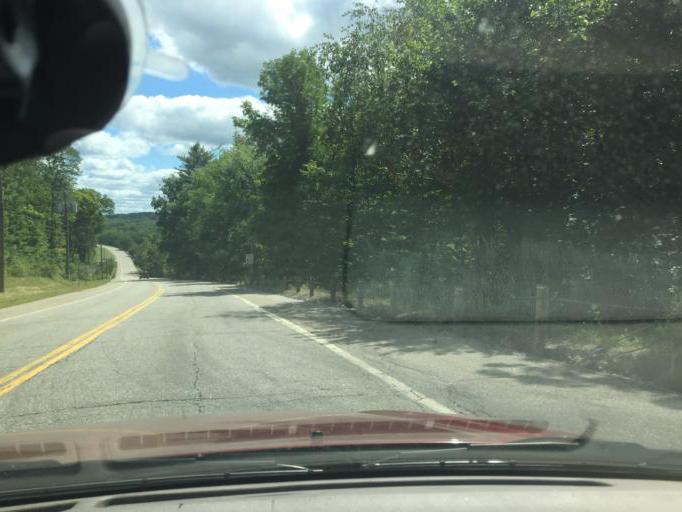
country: US
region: Connecticut
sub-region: Litchfield County
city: Litchfield
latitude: 41.7892
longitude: -73.2105
